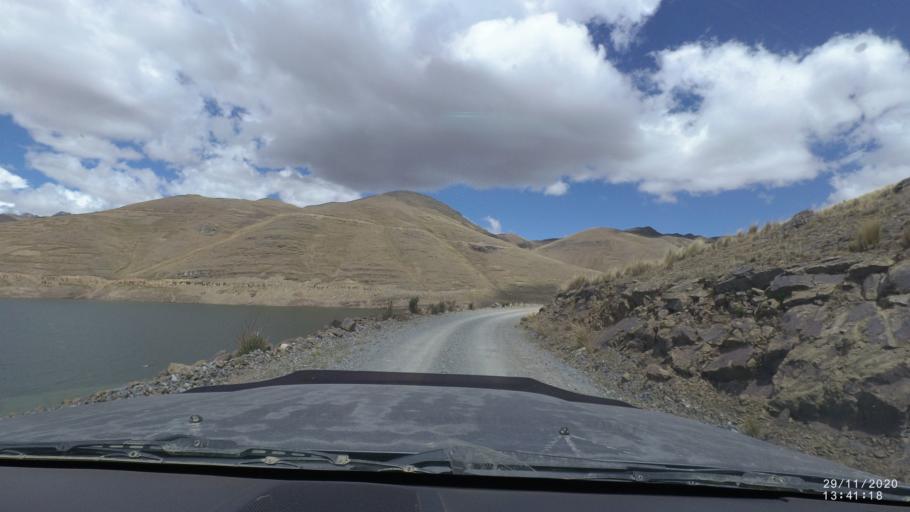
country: BO
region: Cochabamba
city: Cochabamba
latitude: -17.1315
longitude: -66.3248
